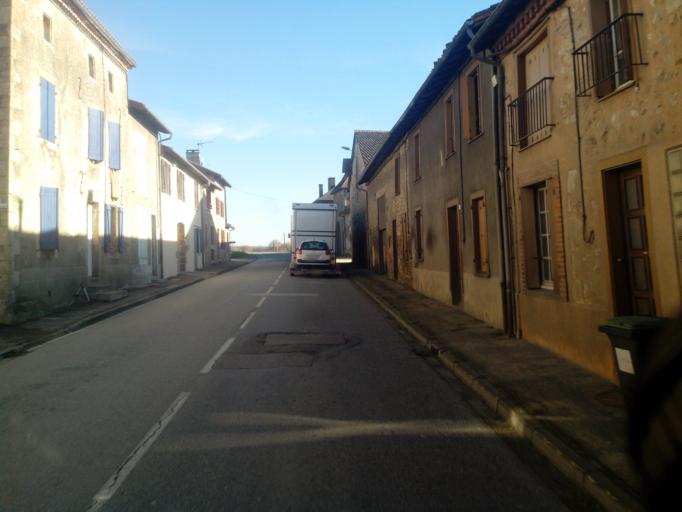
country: FR
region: Limousin
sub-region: Departement de la Haute-Vienne
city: Bellac
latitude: 46.0685
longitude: 1.1066
